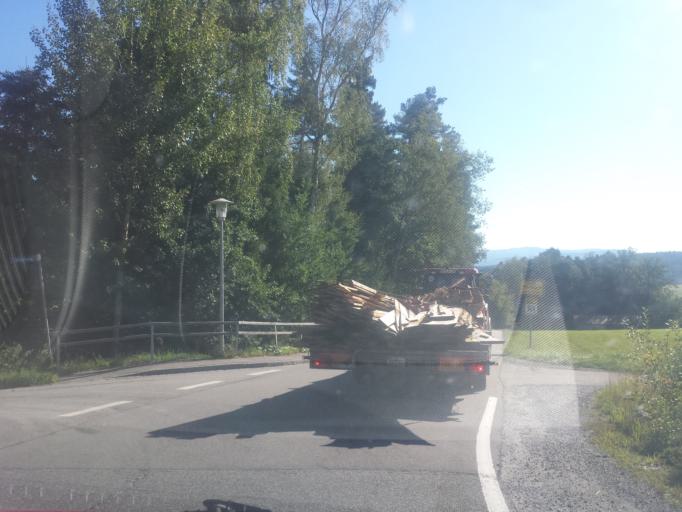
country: DE
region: Bavaria
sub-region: Lower Bavaria
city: Viechtach
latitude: 49.0643
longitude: 12.9013
